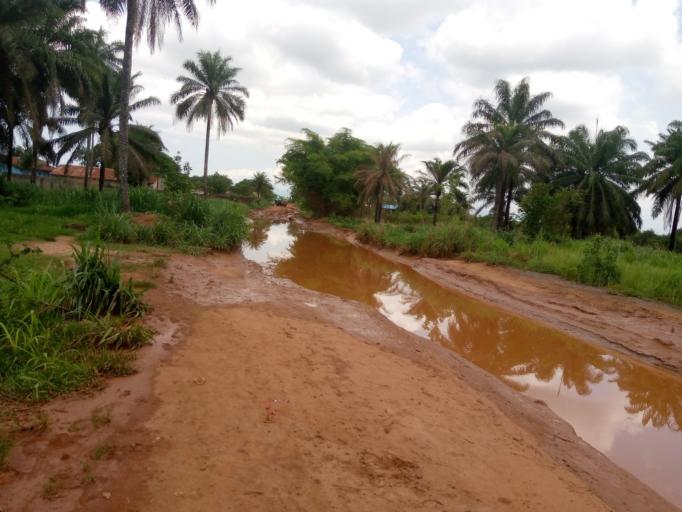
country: SL
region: Western Area
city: Waterloo
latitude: 8.3885
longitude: -12.9503
